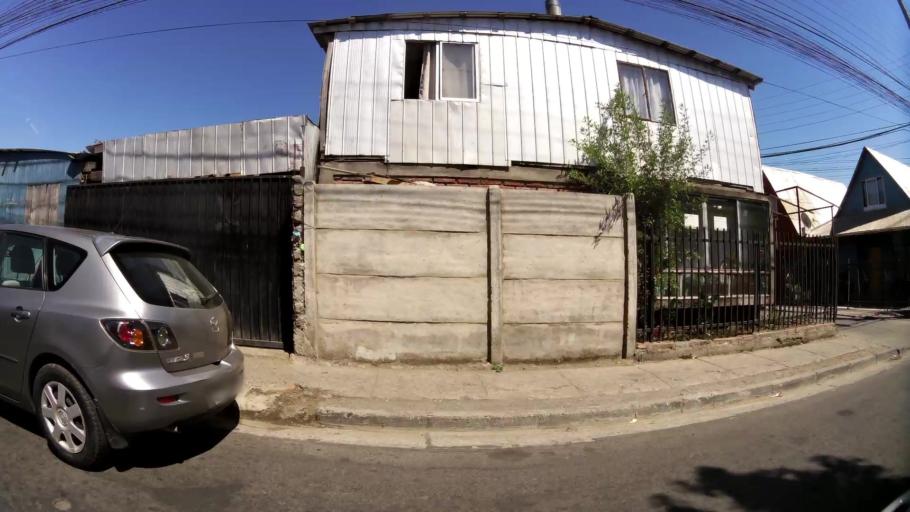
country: CL
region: Maule
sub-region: Provincia de Curico
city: Curico
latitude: -34.9643
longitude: -71.2366
